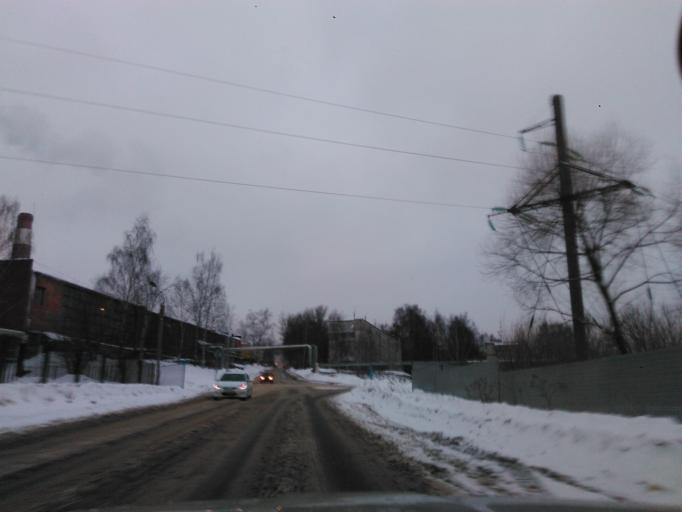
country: RU
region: Moskovskaya
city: Yakhroma
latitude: 56.2788
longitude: 37.4899
